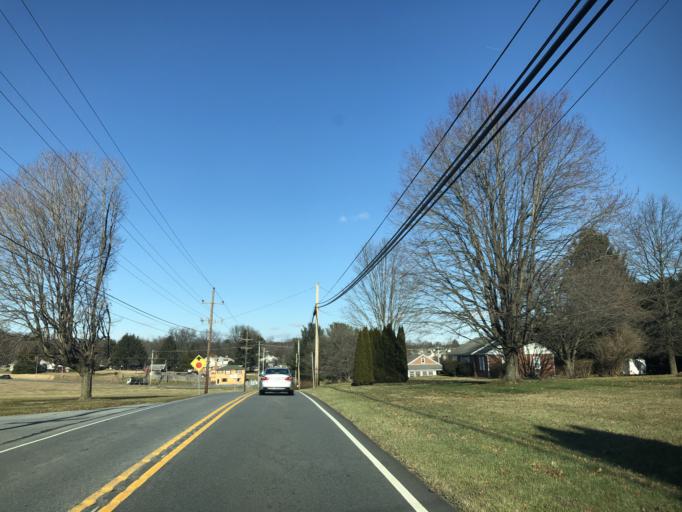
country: US
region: Pennsylvania
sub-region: Chester County
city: South Coatesville
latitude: 39.9528
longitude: -75.8417
